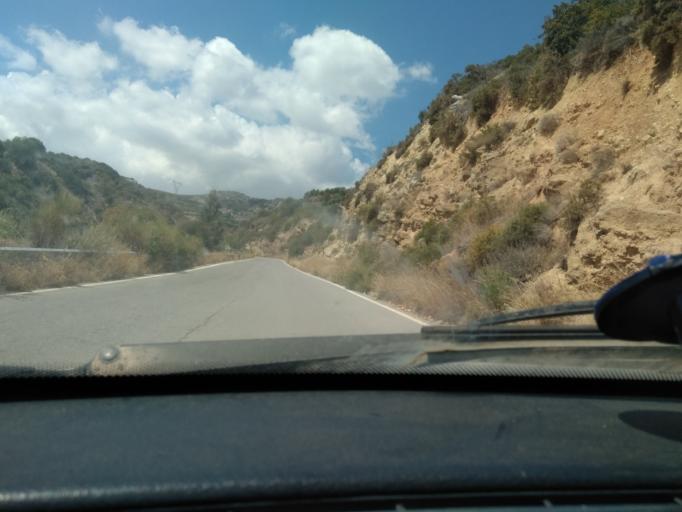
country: GR
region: Crete
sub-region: Nomos Lasithiou
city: Siteia
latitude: 35.1412
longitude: 26.0775
